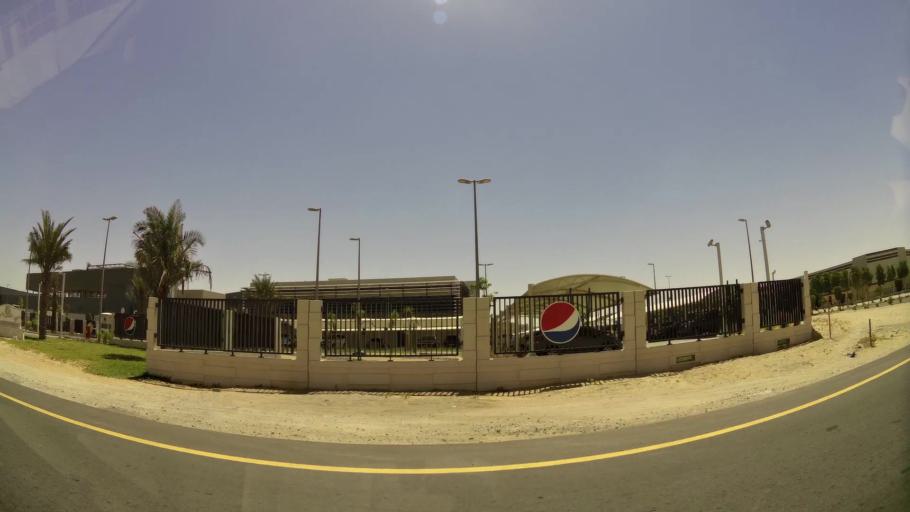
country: AE
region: Dubai
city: Dubai
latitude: 24.9738
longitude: 55.1940
